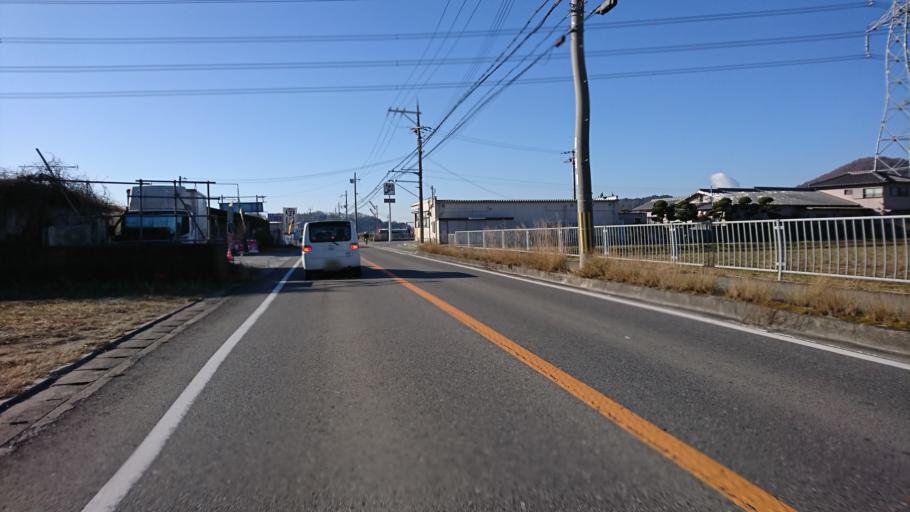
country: JP
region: Hyogo
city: Kakogawacho-honmachi
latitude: 34.8300
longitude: 134.8381
